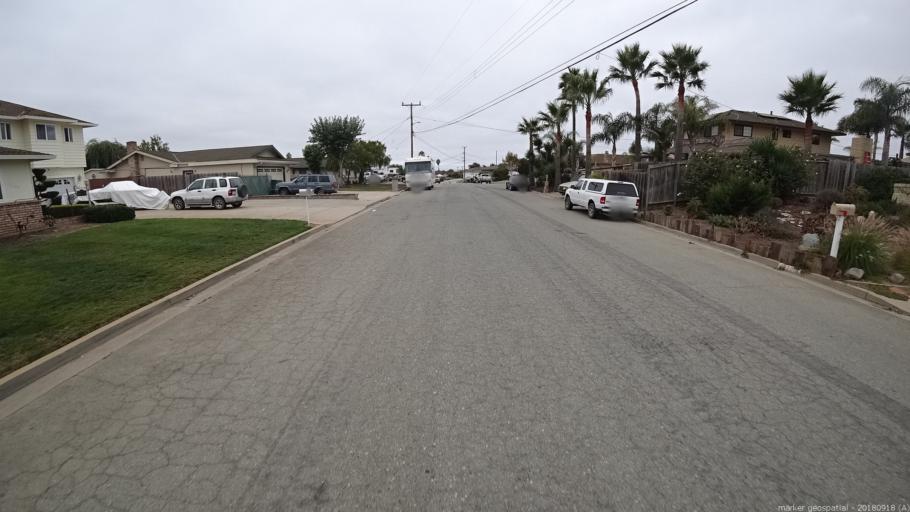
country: US
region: California
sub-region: Monterey County
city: Prunedale
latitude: 36.7375
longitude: -121.6407
